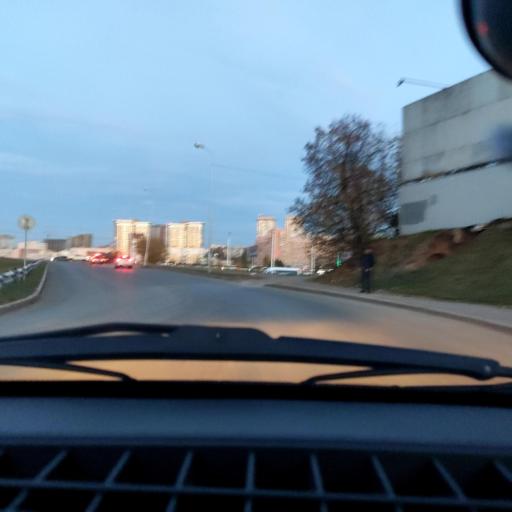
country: RU
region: Bashkortostan
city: Ufa
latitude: 54.7198
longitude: 55.9759
